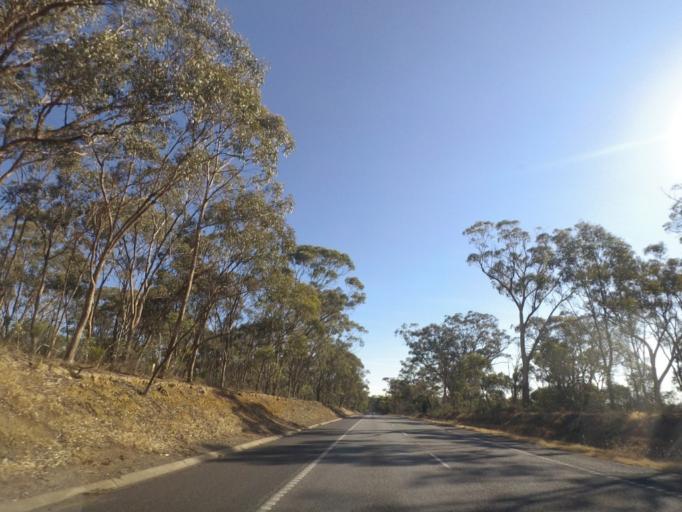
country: AU
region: Victoria
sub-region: Murrindindi
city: Kinglake West
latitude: -37.1746
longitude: 145.0735
